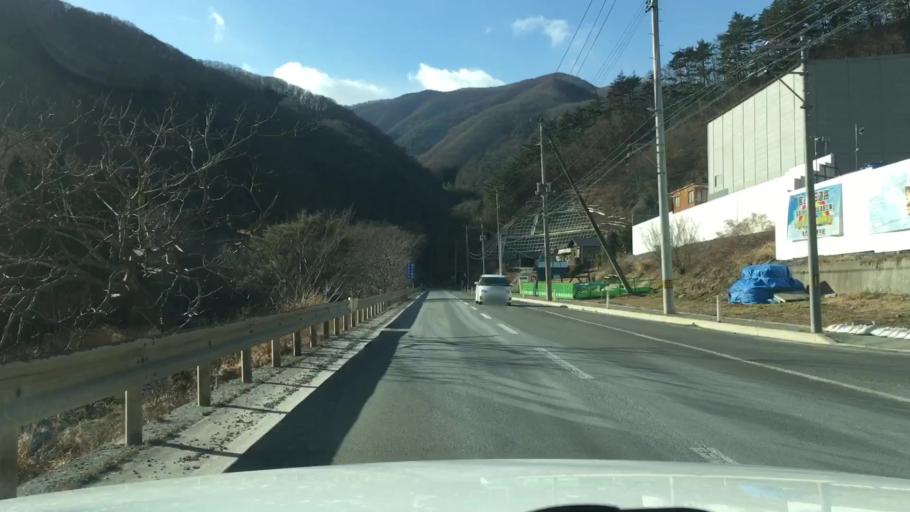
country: JP
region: Iwate
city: Miyako
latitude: 39.5966
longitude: 141.6559
